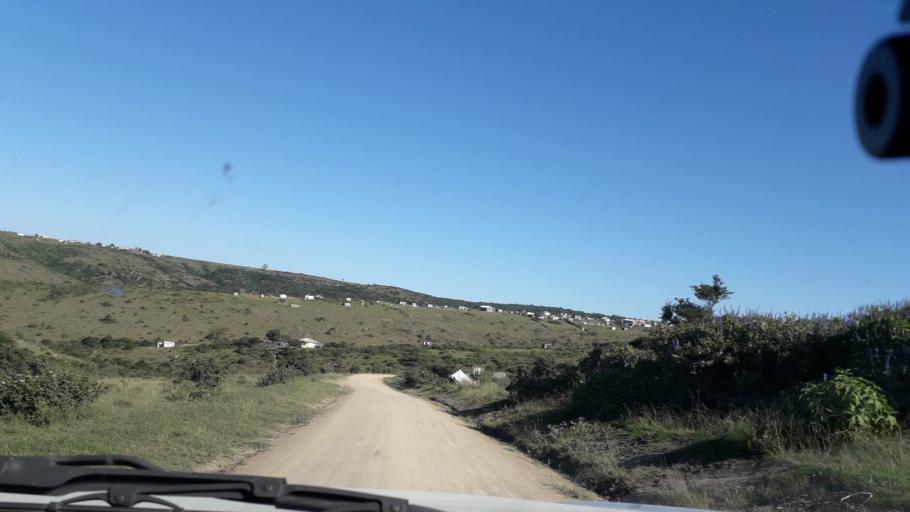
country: ZA
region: Eastern Cape
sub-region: Buffalo City Metropolitan Municipality
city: East London
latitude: -32.7984
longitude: 27.9690
